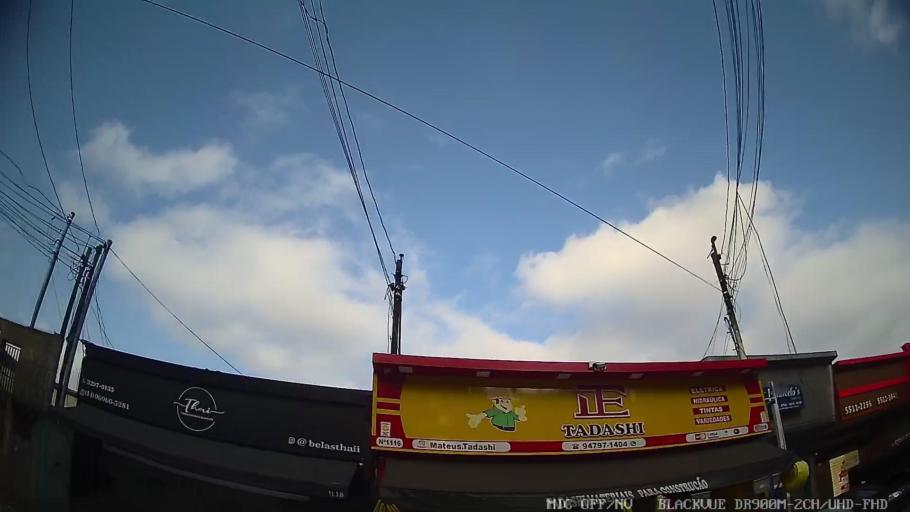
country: BR
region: Sao Paulo
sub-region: Taboao Da Serra
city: Taboao da Serra
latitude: -23.6470
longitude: -46.7636
